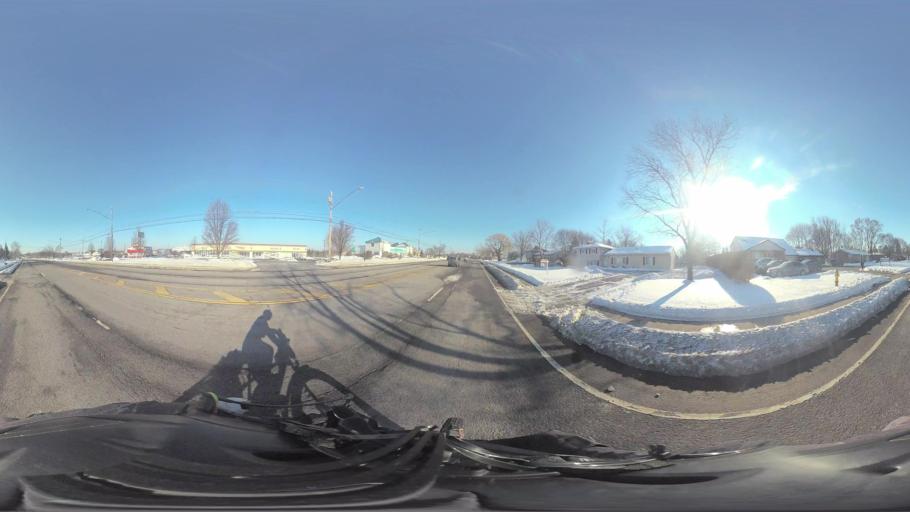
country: US
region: New York
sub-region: Monroe County
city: Rochester
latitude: 43.0662
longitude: -77.6086
